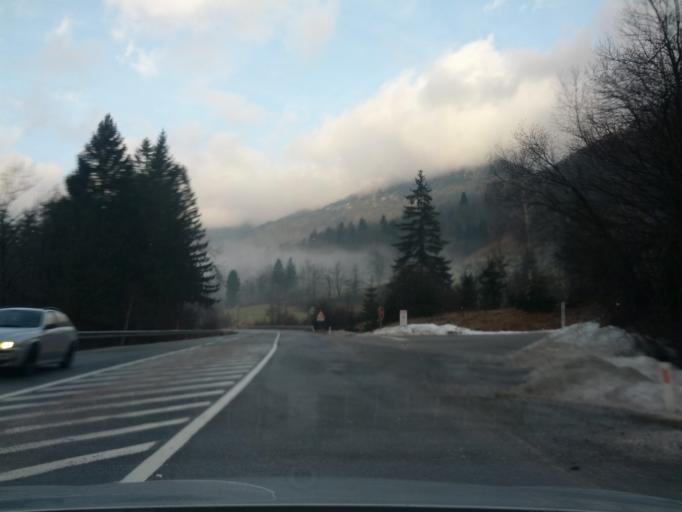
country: SI
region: Jesenice
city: Hrusica
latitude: 46.4564
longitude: 13.9790
